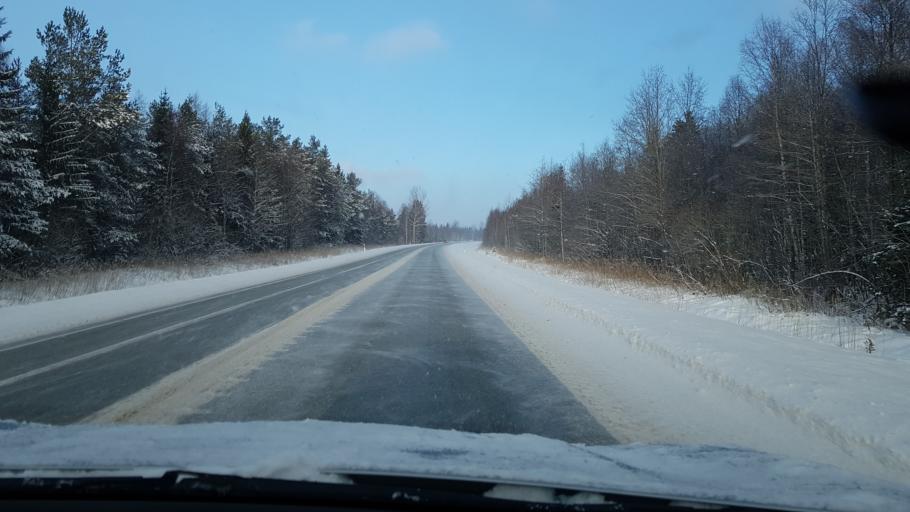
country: EE
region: Harju
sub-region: Nissi vald
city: Riisipere
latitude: 59.1564
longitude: 24.3411
